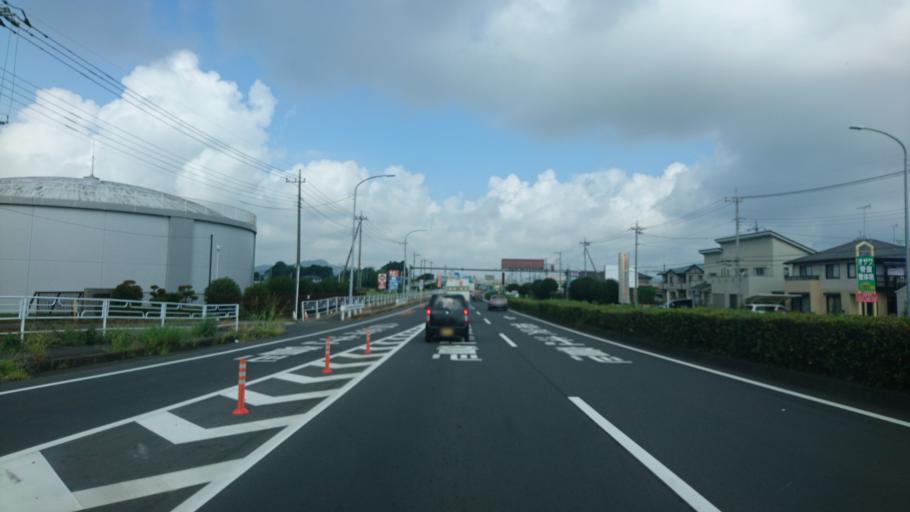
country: JP
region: Tochigi
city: Ashikaga
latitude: 36.3131
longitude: 139.4321
